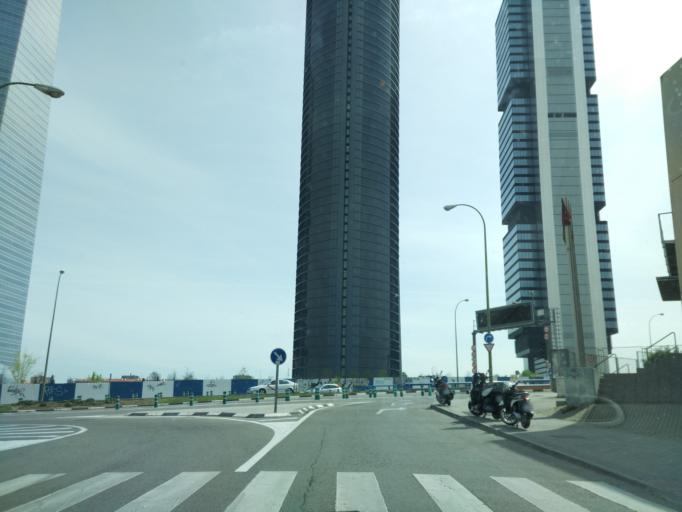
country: ES
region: Madrid
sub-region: Provincia de Madrid
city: Chamartin
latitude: 40.4771
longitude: -3.6913
